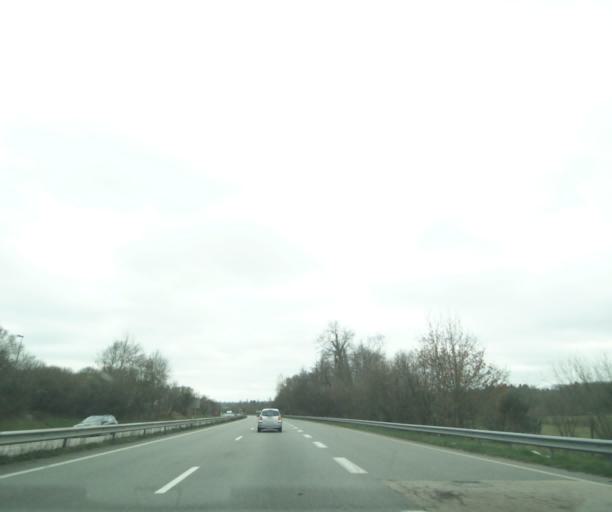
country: FR
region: Limousin
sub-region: Departement de la Haute-Vienne
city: Rilhac-Rancon
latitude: 45.9092
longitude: 1.2918
